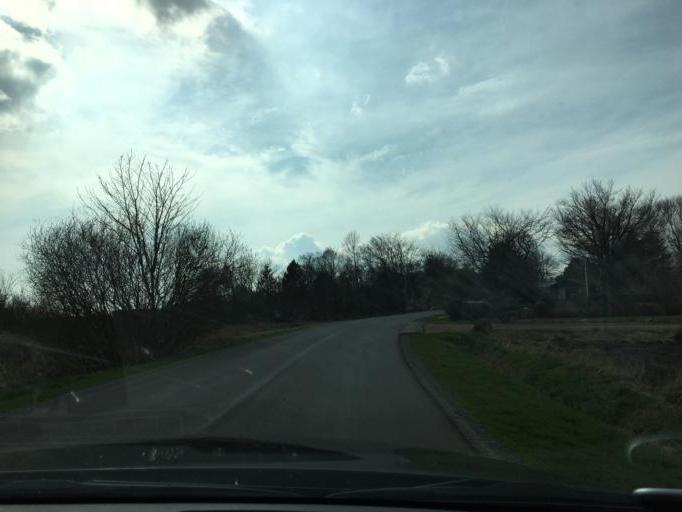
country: DK
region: South Denmark
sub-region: Esbjerg Kommune
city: Bramming
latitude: 55.4875
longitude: 8.6487
